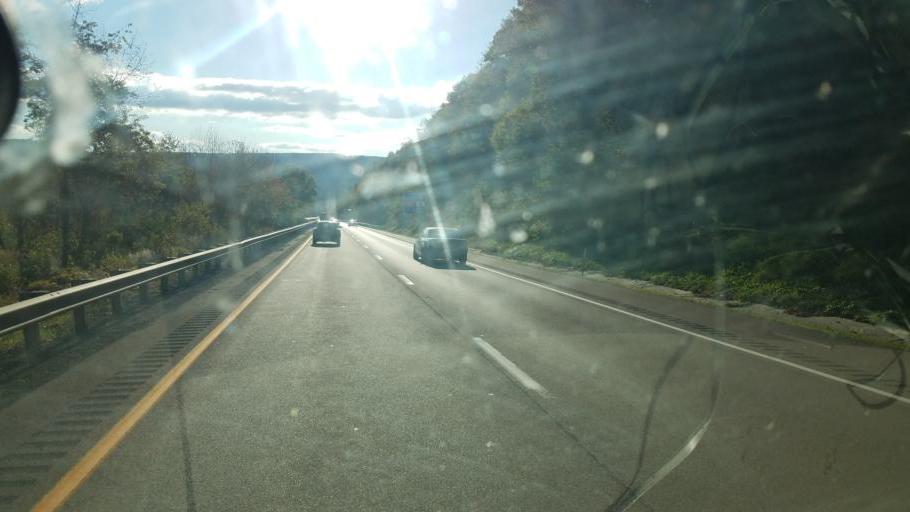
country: US
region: Maryland
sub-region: Allegany County
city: La Vale
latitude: 39.6385
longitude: -78.8605
